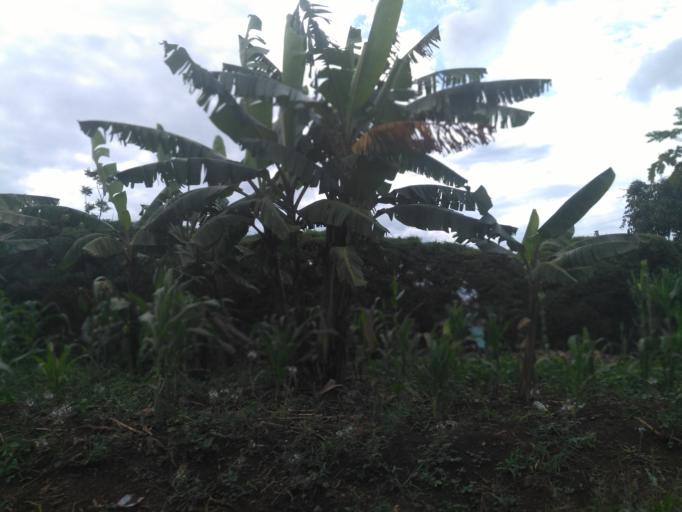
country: UG
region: Central Region
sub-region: Buikwe District
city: Njeru
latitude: 0.4196
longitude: 33.1859
